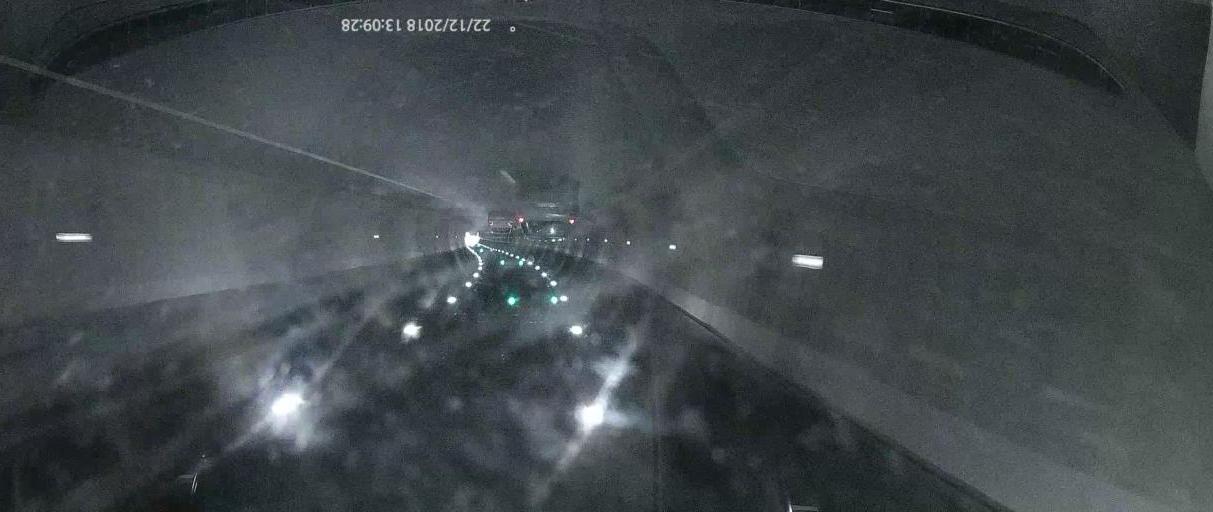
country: BG
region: Sofiya
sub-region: Obshtina Botevgrad
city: Botevgrad
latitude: 42.8556
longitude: 23.7906
